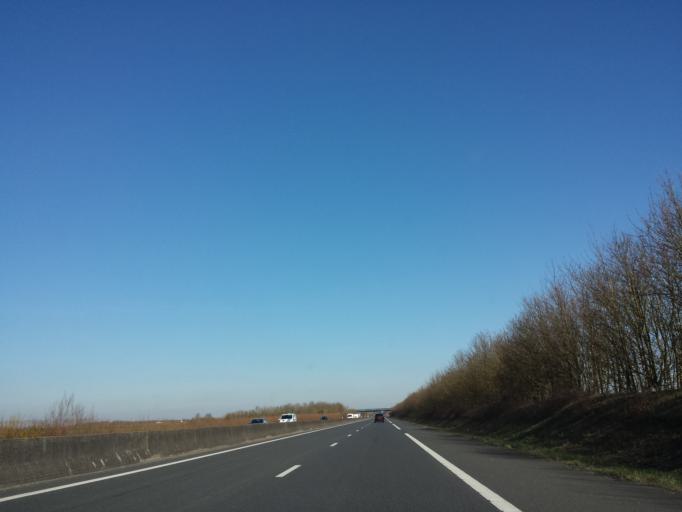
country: FR
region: Picardie
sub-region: Departement de l'Oise
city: Tille
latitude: 49.4773
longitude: 2.1637
